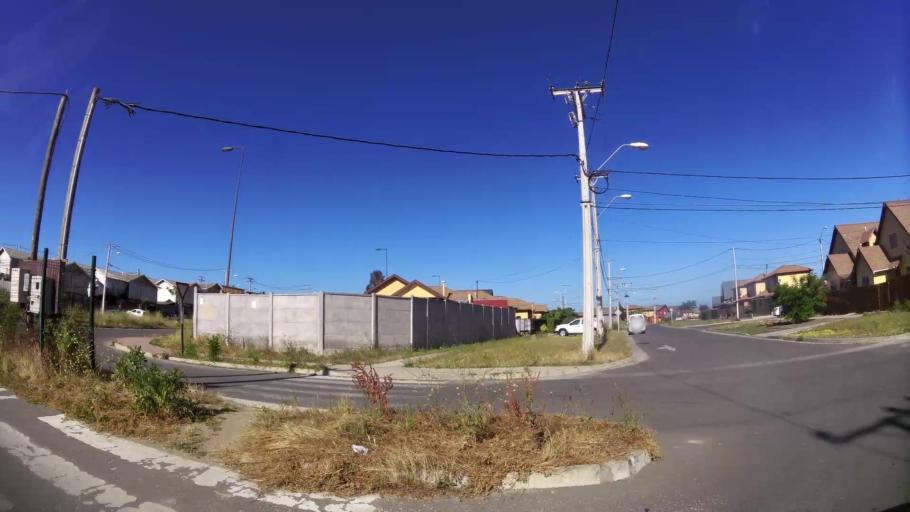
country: CL
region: Valparaiso
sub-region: Provincia de Valparaiso
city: Valparaiso
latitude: -33.1212
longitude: -71.5847
